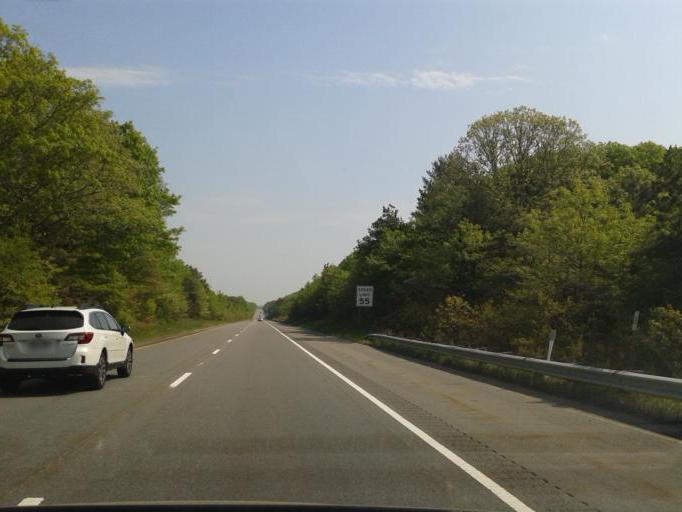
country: US
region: Massachusetts
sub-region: Barnstable County
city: North Falmouth
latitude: 41.6239
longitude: -70.6157
